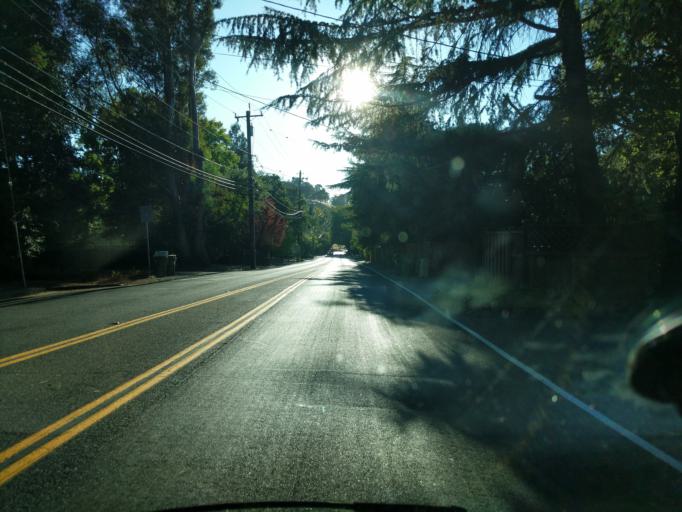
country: US
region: California
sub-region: Contra Costa County
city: Diablo
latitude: 37.8320
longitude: -121.9532
